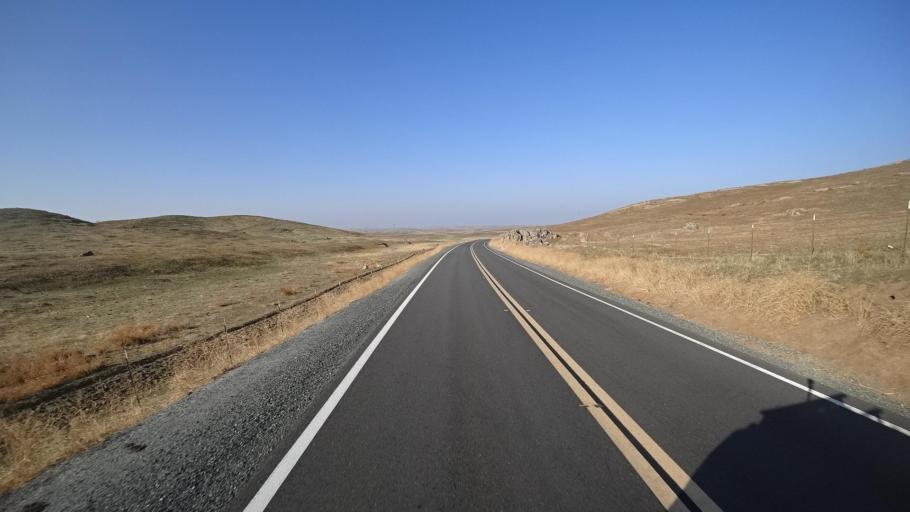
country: US
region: California
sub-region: Tulare County
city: Richgrove
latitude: 35.7418
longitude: -118.9098
